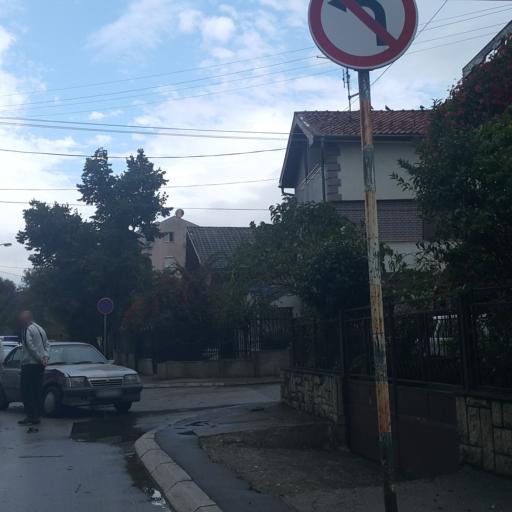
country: RS
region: Central Serbia
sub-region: Rasinski Okrug
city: Krusevac
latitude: 43.5803
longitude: 21.3333
